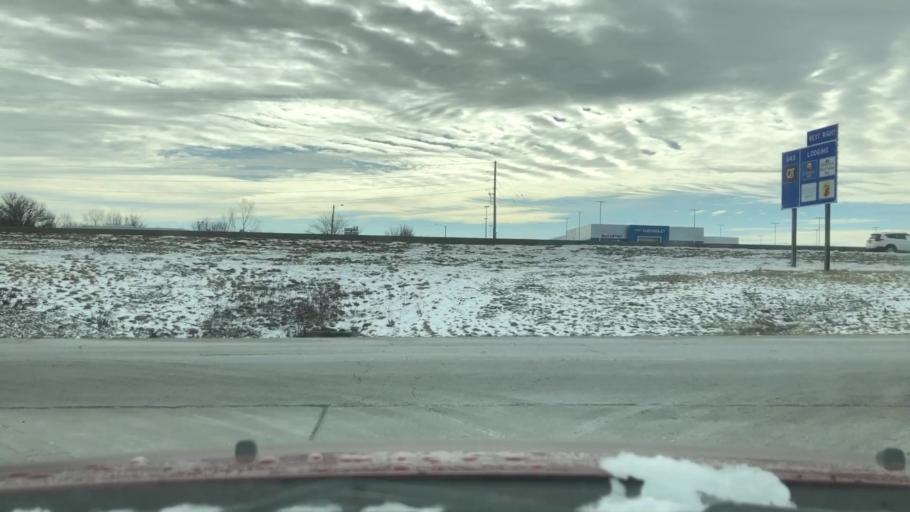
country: US
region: Missouri
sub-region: Jackson County
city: Lees Summit
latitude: 38.9046
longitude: -94.3552
